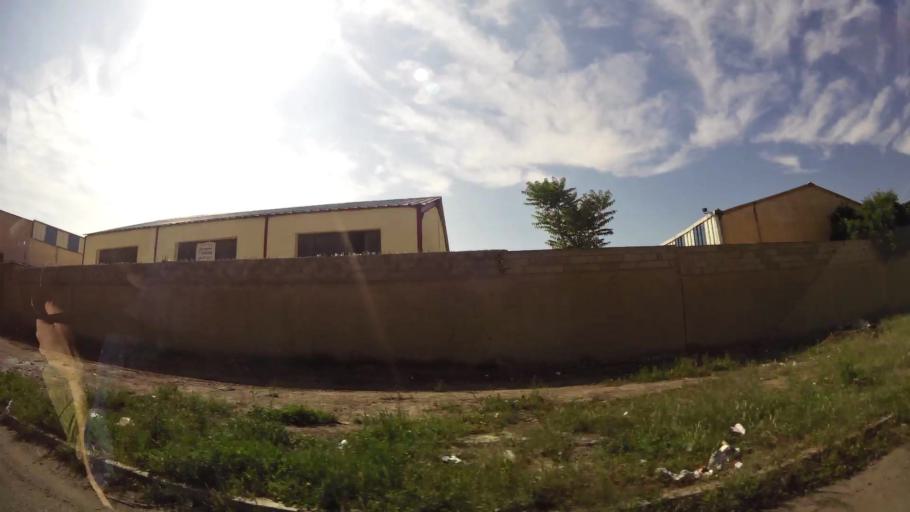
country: MA
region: Oriental
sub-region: Oujda-Angad
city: Oujda
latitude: 34.7056
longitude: -1.8882
